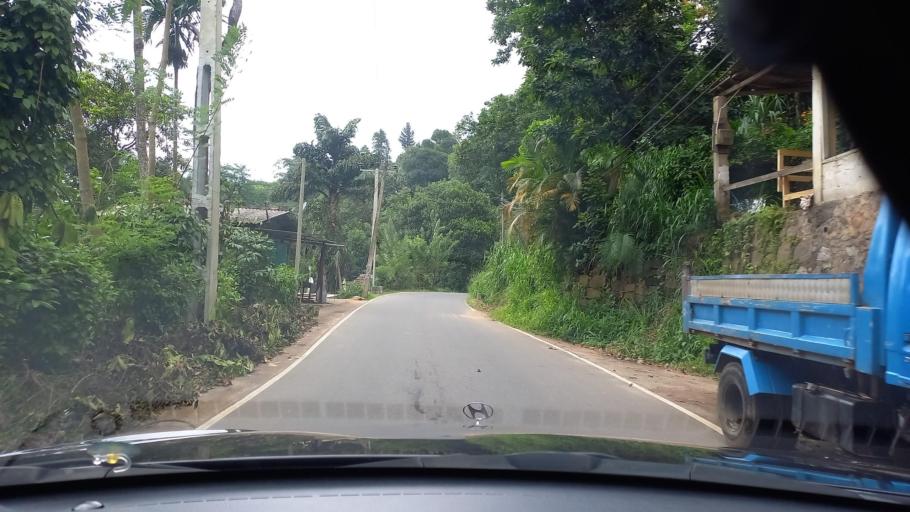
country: LK
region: Central
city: Gampola
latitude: 7.2280
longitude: 80.6060
